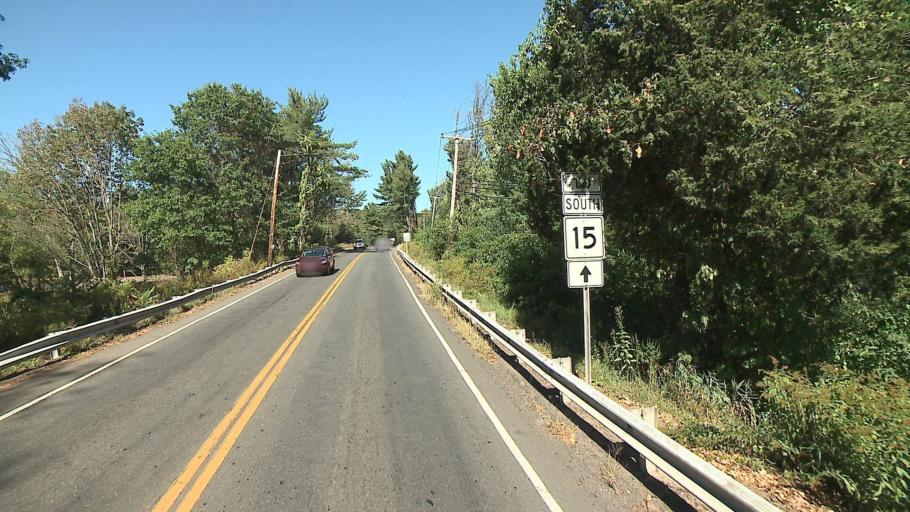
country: US
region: Connecticut
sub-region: New Haven County
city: Orange
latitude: 41.2863
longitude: -73.0410
